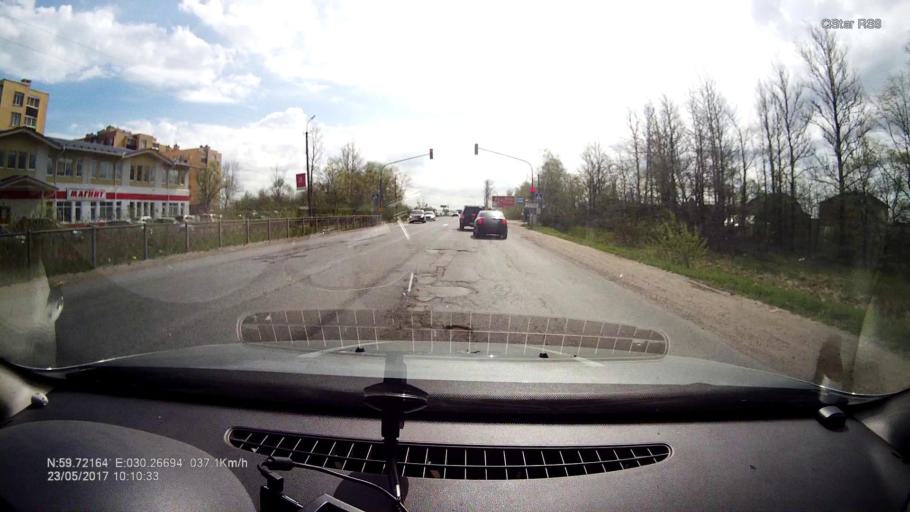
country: RU
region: St.-Petersburg
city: Aleksandrovskaya
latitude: 59.7216
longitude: 30.2671
